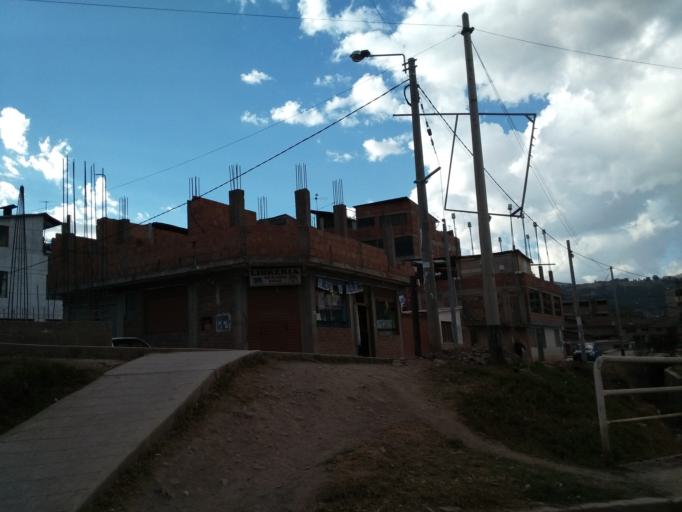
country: PE
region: Cusco
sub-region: Provincia de Cusco
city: Cusco
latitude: -13.5394
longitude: -71.9492
